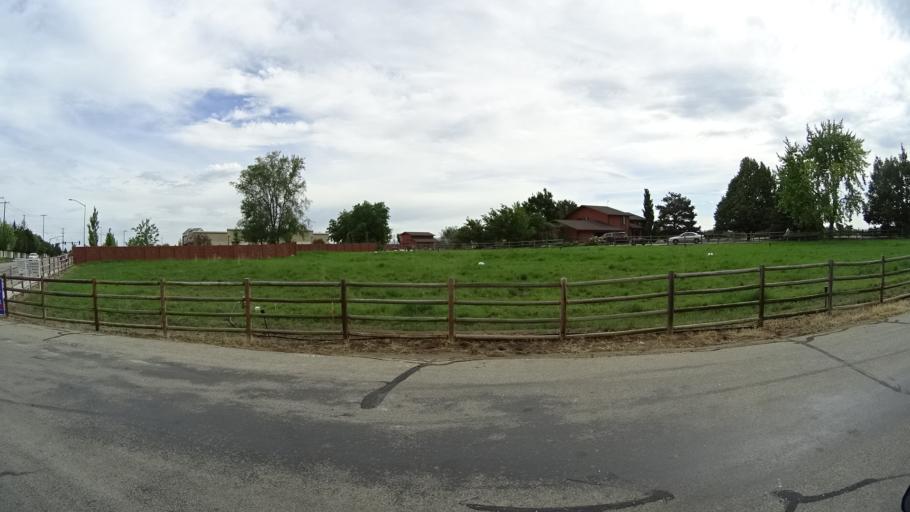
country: US
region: Idaho
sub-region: Ada County
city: Meridian
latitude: 43.5739
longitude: -116.3542
